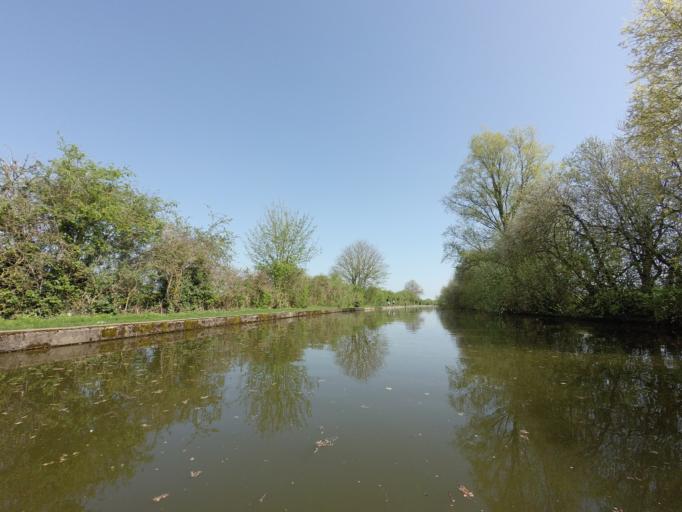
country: GB
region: England
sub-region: Buckinghamshire
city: Cheddington
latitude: 51.8271
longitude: -0.6631
